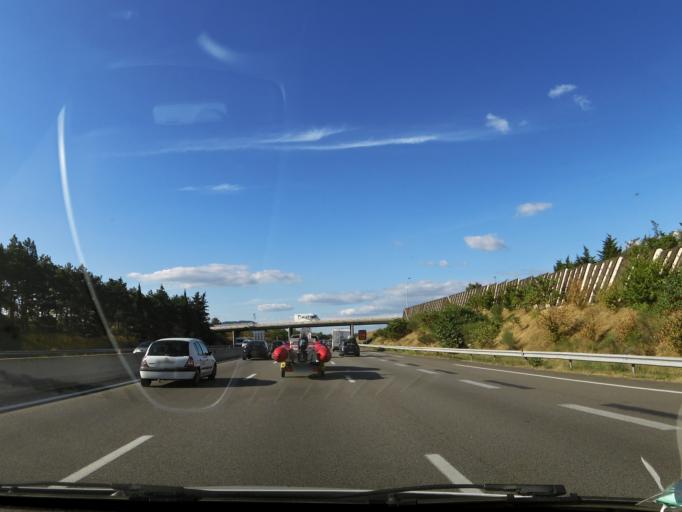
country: FR
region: Rhone-Alpes
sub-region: Departement de la Drome
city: Portes-les-Valence
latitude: 44.8699
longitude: 4.8650
